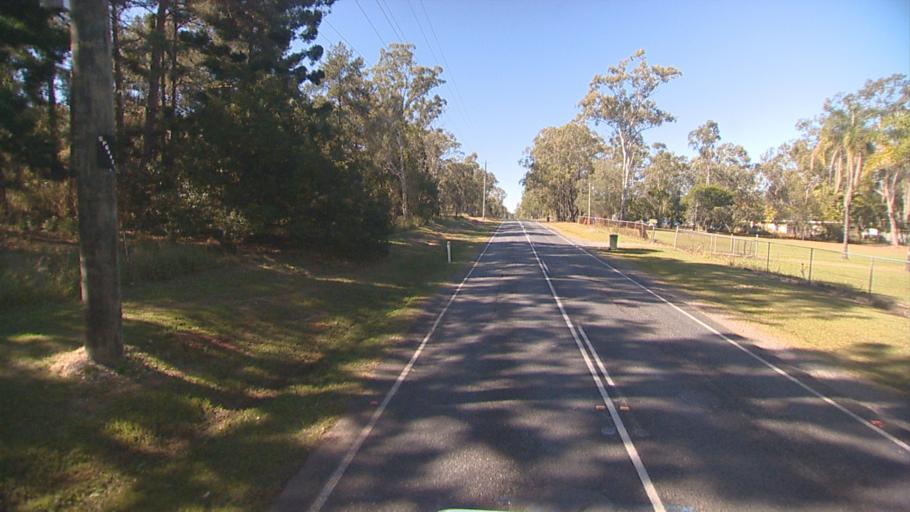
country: AU
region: Queensland
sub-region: Logan
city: Park Ridge South
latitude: -27.7174
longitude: 153.0471
